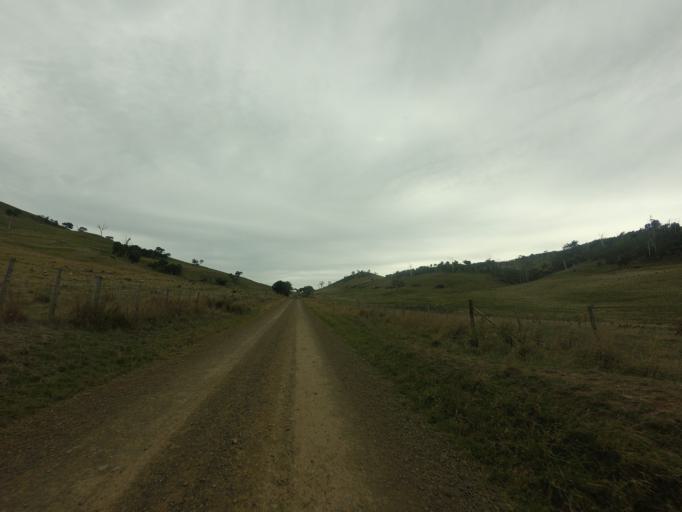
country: AU
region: Tasmania
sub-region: Derwent Valley
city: New Norfolk
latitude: -42.3775
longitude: 146.8653
